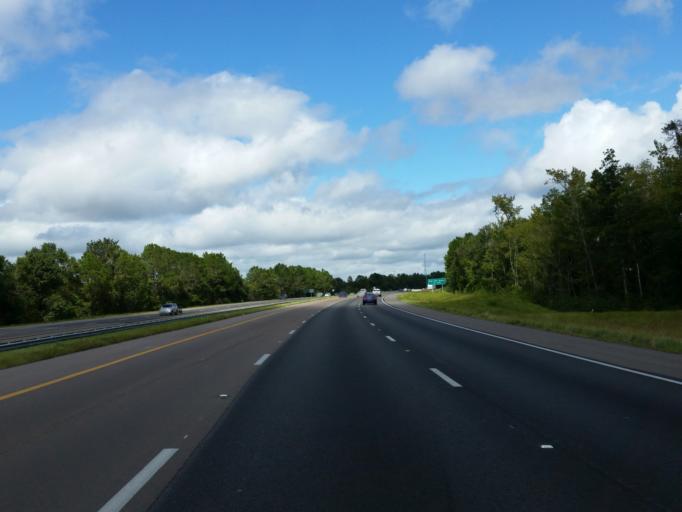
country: US
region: Florida
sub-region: Hillsborough County
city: Pebble Creek
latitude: 28.1574
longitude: -82.3923
